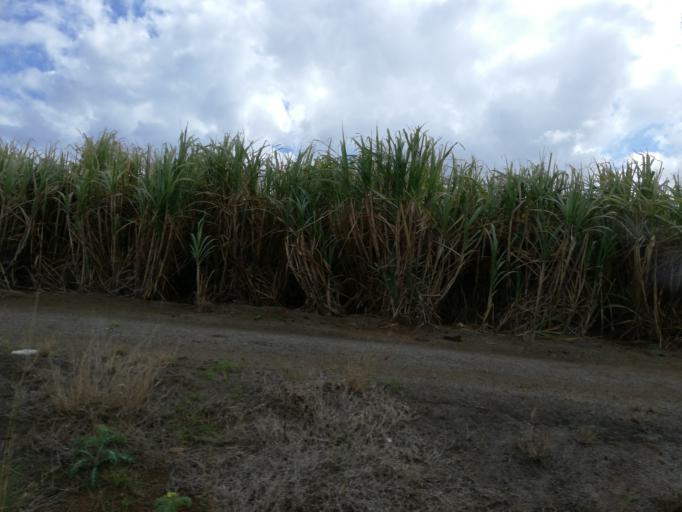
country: MU
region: Pamplemousses
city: Arsenal
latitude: -20.1026
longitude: 57.5446
